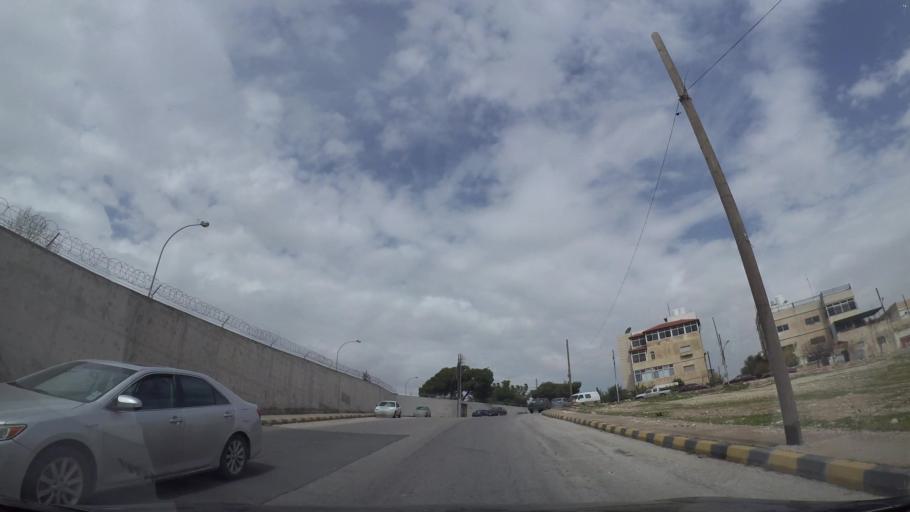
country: JO
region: Amman
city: Amman
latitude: 31.9623
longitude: 35.9487
